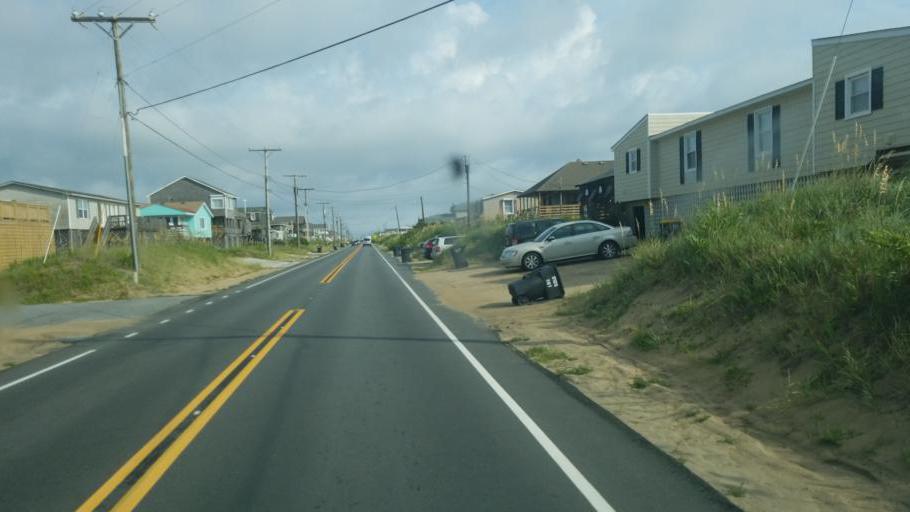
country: US
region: North Carolina
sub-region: Dare County
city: Kill Devil Hills
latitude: 36.0505
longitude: -75.6795
